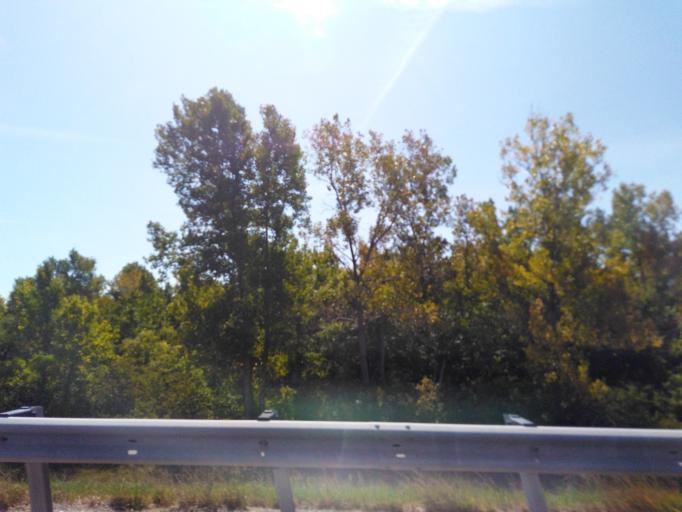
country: US
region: Illinois
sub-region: Saint Clair County
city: Cahokia
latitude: 38.5377
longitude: -90.1838
